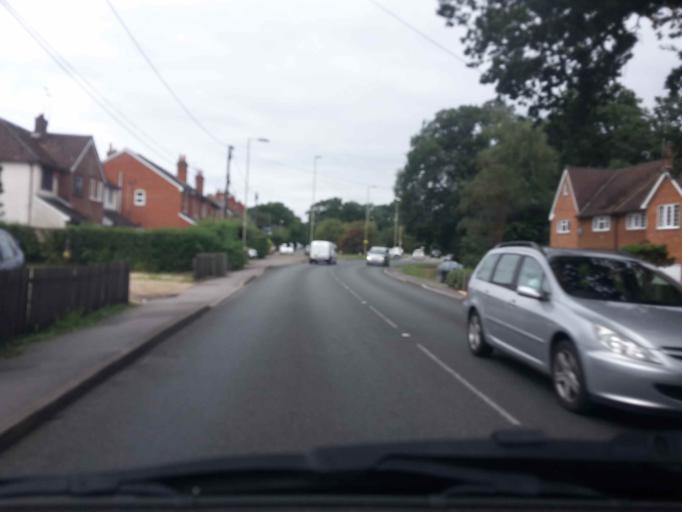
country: GB
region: England
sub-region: Hampshire
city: Fleet
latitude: 51.2919
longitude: -0.8225
